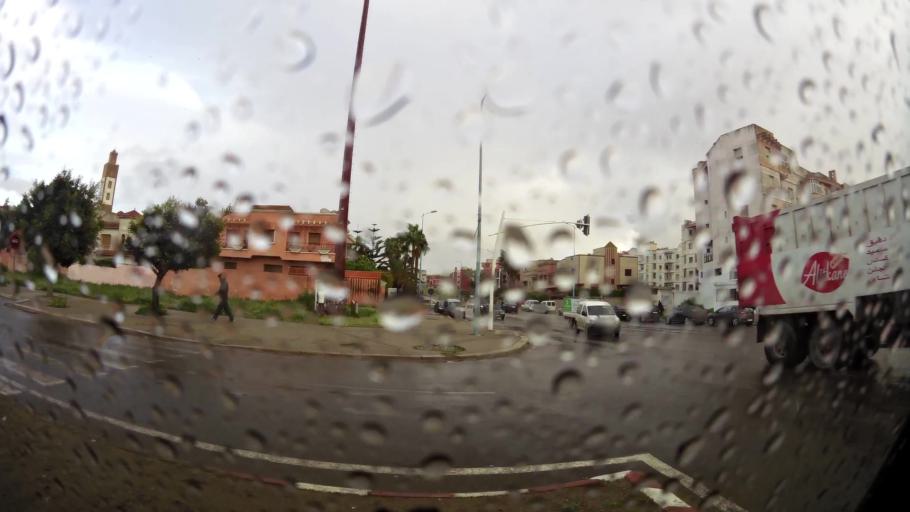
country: MA
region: Doukkala-Abda
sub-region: El-Jadida
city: El Jadida
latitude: 33.2397
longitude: -8.5293
